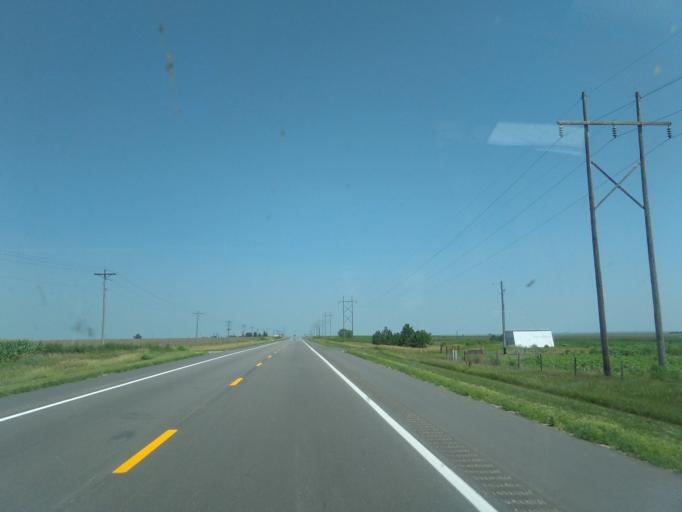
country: US
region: Nebraska
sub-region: Red Willow County
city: McCook
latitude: 40.2733
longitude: -100.6500
